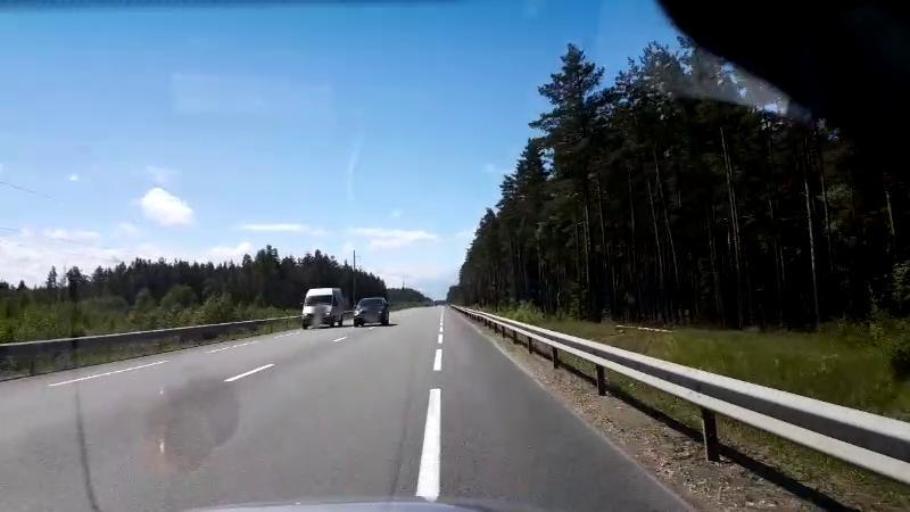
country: LV
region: Saulkrastu
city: Saulkrasti
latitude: 57.2176
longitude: 24.4030
